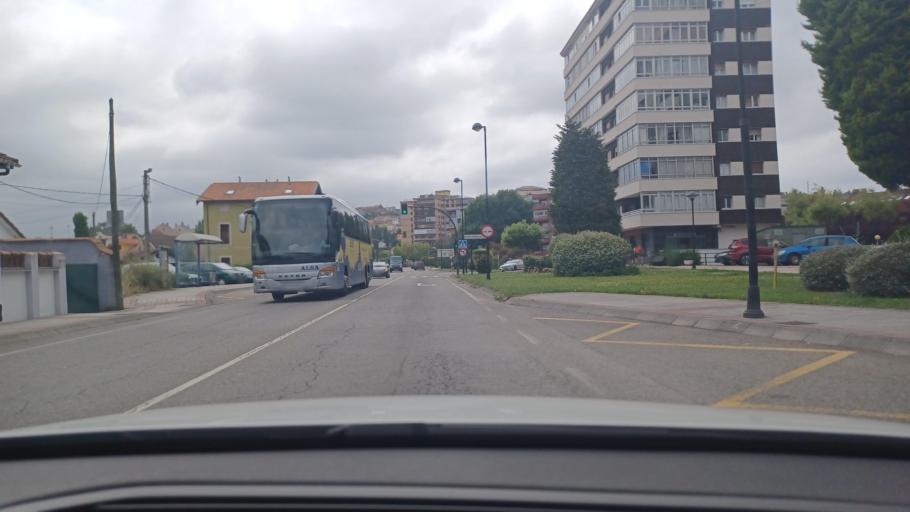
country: ES
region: Asturias
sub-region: Province of Asturias
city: Aviles
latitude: 43.5718
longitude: -5.9571
